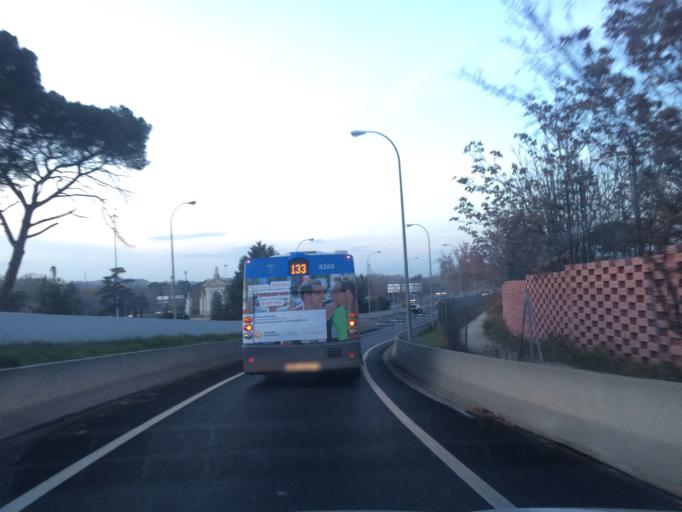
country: ES
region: Madrid
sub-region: Provincia de Madrid
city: Moncloa-Aravaca
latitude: 40.4545
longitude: -3.7424
